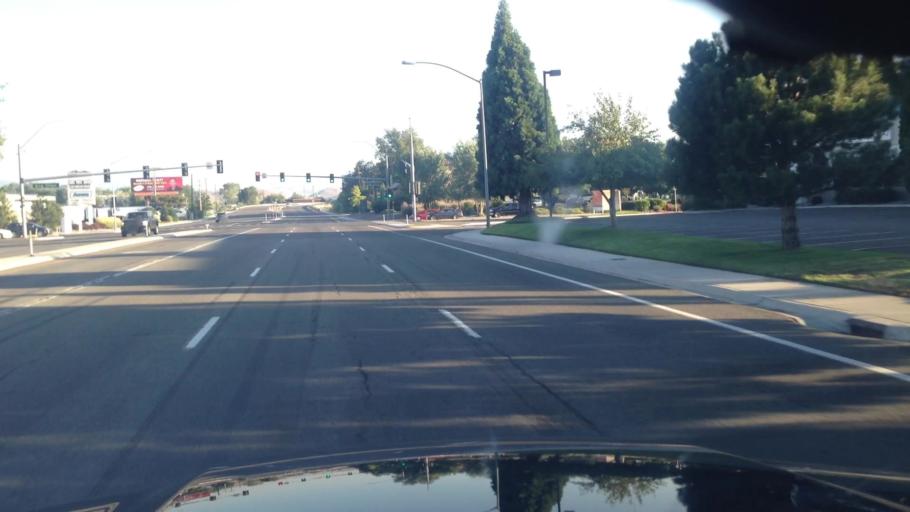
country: US
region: Nevada
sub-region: Washoe County
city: Sparks
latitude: 39.5225
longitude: -119.7402
